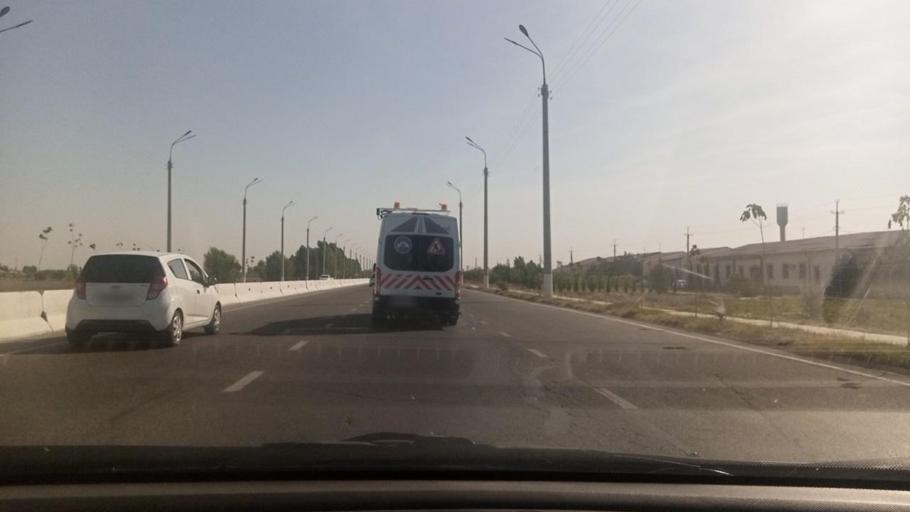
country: UZ
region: Toshkent Shahri
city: Bektemir
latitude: 41.2067
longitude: 69.3389
